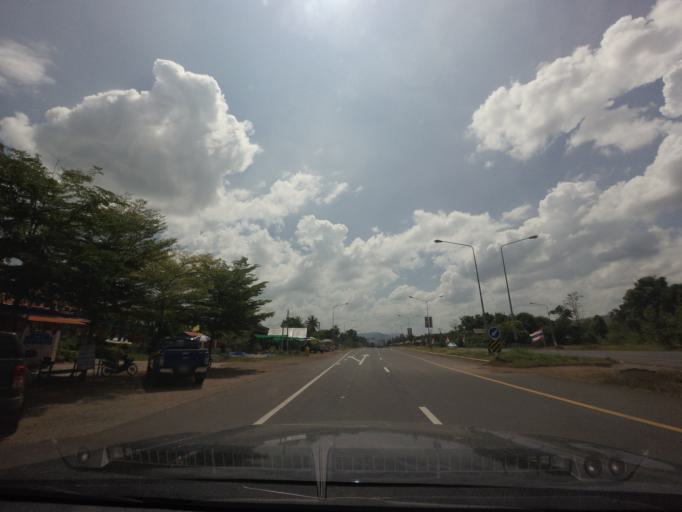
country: TH
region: Phetchabun
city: Phetchabun
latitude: 16.4430
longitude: 101.1086
